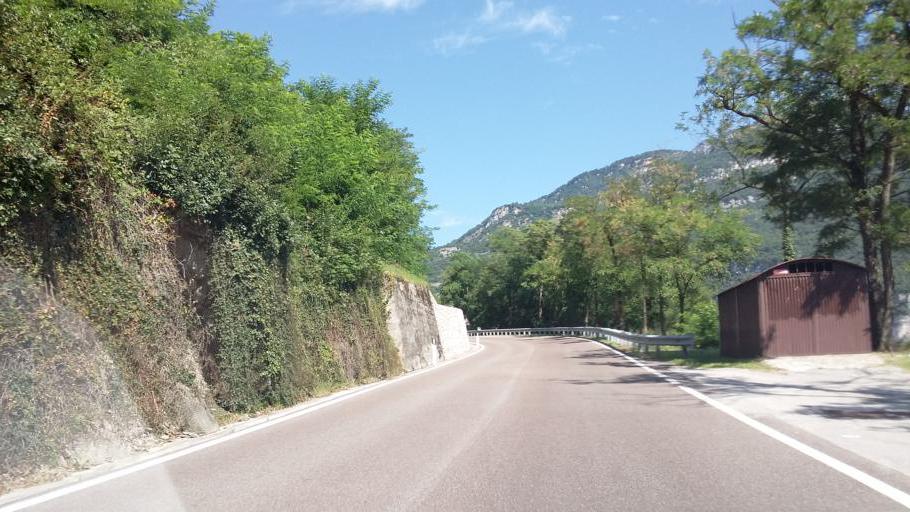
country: IT
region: Trentino-Alto Adige
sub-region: Provincia di Trento
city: Mori
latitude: 45.8436
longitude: 10.9739
